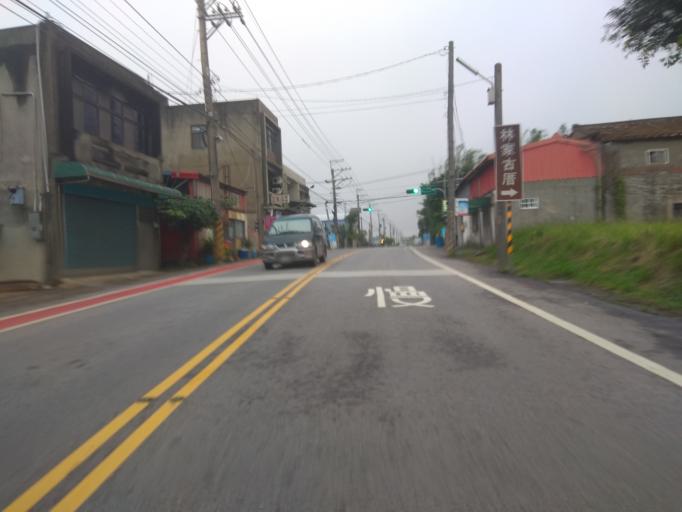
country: TW
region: Taiwan
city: Taoyuan City
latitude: 25.0039
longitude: 121.1276
